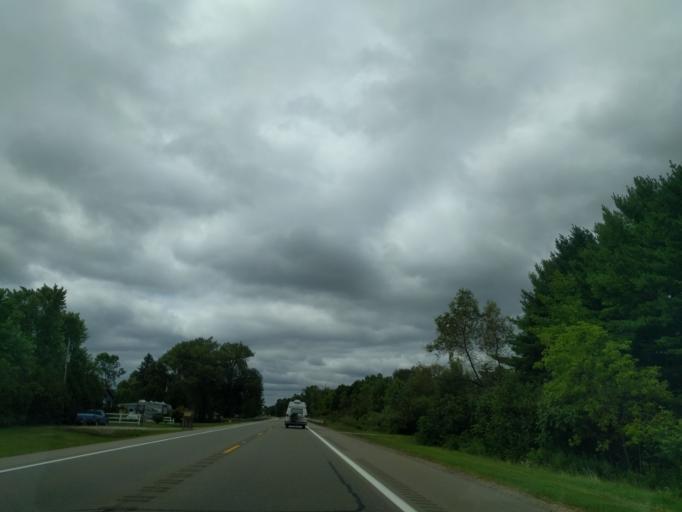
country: US
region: Michigan
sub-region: Menominee County
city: Menominee
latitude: 45.2567
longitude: -87.4812
